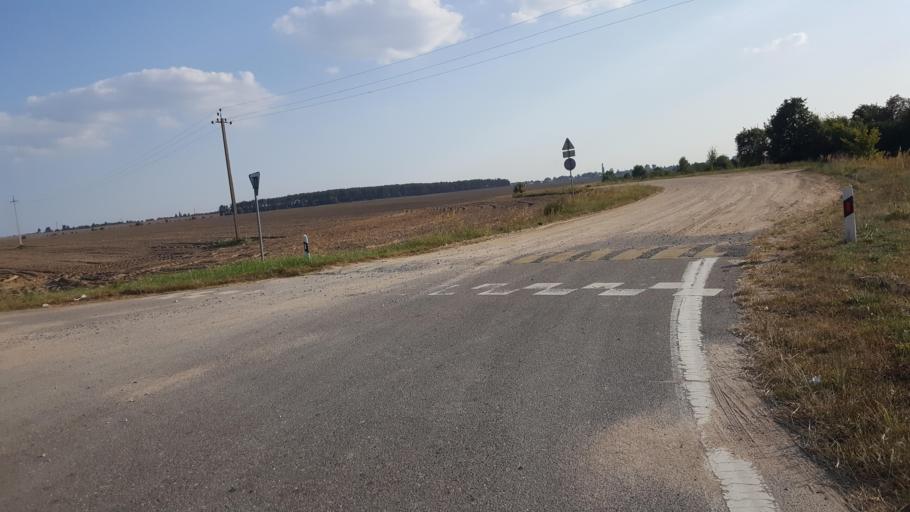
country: BY
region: Brest
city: Kamyanyets
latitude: 52.4208
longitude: 23.8428
